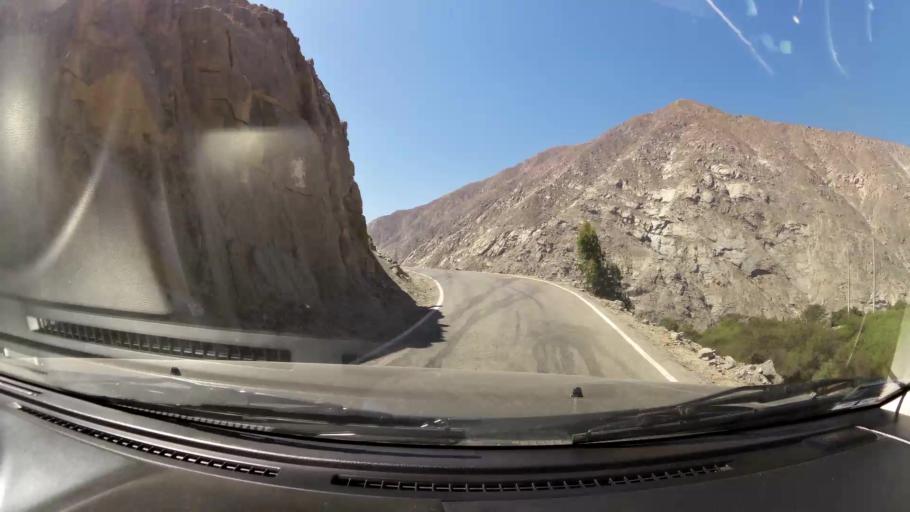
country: PE
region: Ica
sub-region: Provincia de Pisco
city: Huancano
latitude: -13.8254
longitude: -75.5393
